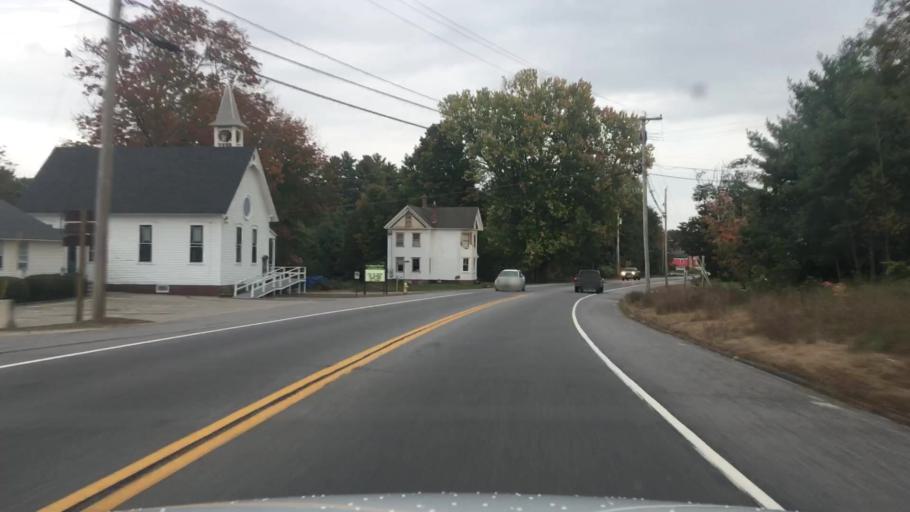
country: US
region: Maine
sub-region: York County
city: Waterboro
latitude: 43.5719
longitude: -70.6795
